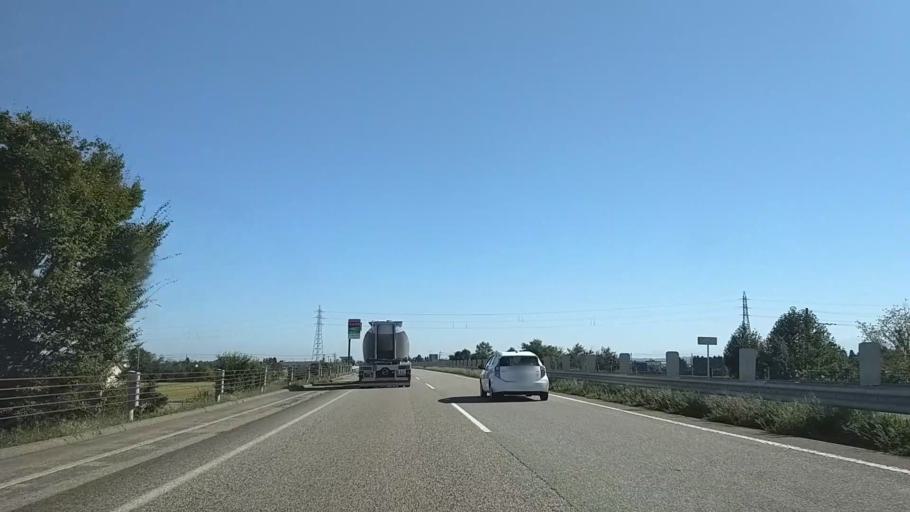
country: JP
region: Toyama
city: Nanto-shi
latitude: 36.6280
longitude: 136.9615
